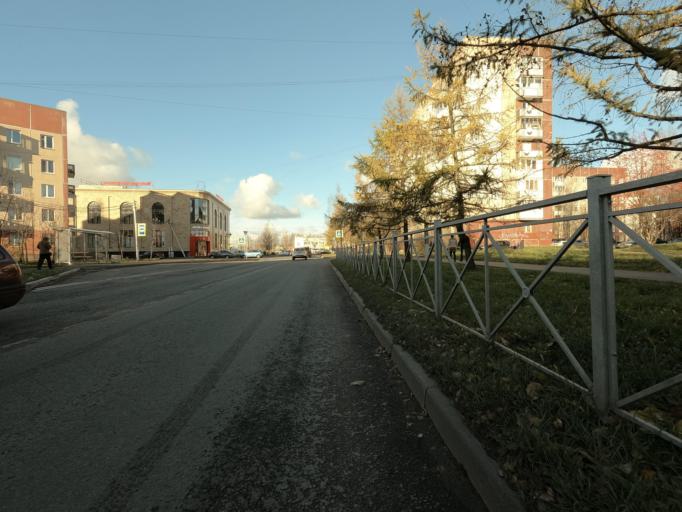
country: RU
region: Leningrad
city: Vsevolozhsk
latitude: 60.0306
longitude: 30.6296
